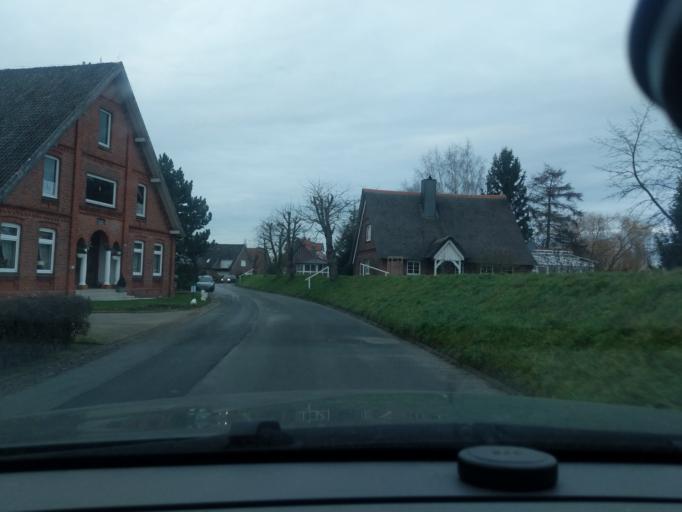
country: DE
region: Lower Saxony
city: Mittelnkirchen
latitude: 53.5331
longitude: 9.6129
